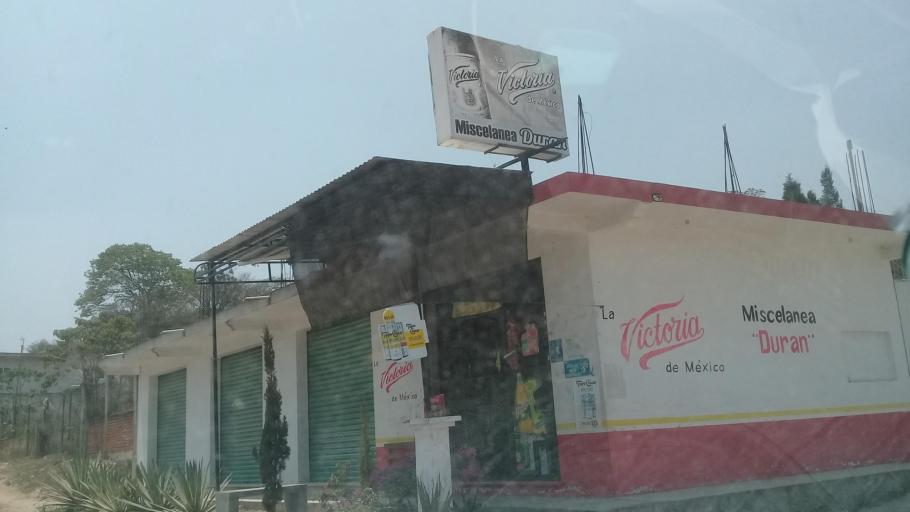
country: MX
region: Veracruz
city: El Castillo
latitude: 19.5546
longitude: -96.8547
